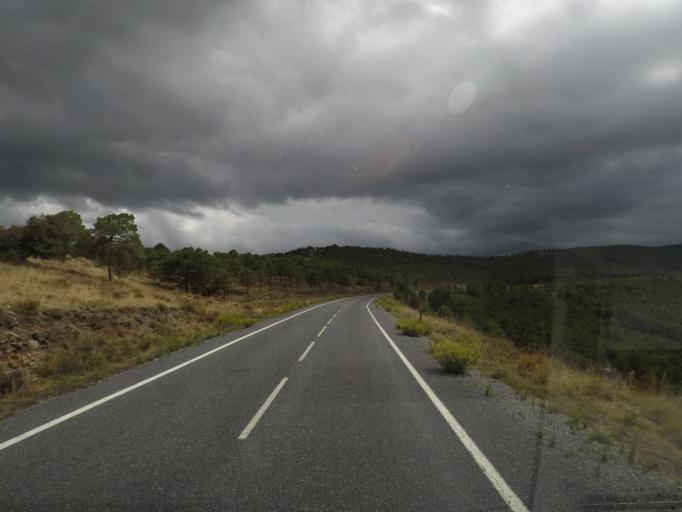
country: ES
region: Andalusia
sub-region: Provincia de Granada
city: Aldeire
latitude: 37.1496
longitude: -3.0500
